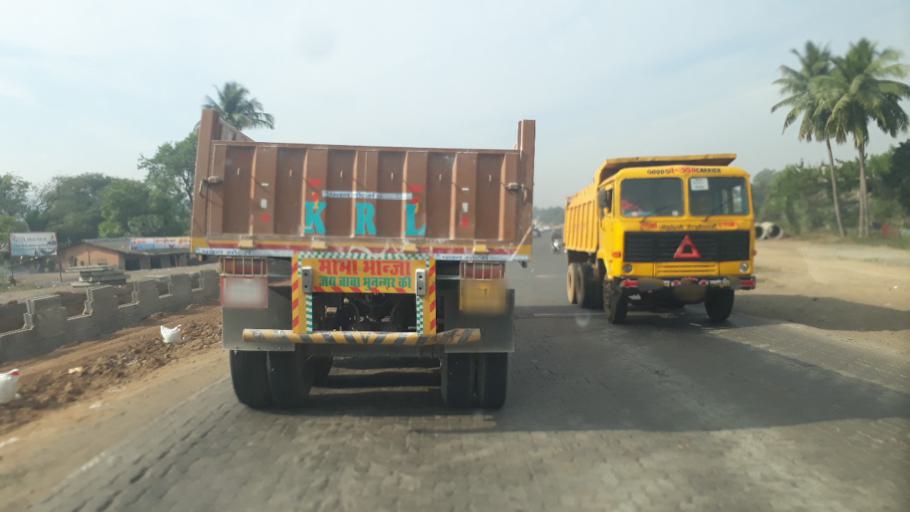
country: IN
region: Maharashtra
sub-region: Raigarh
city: Pen
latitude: 18.7225
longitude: 73.0685
